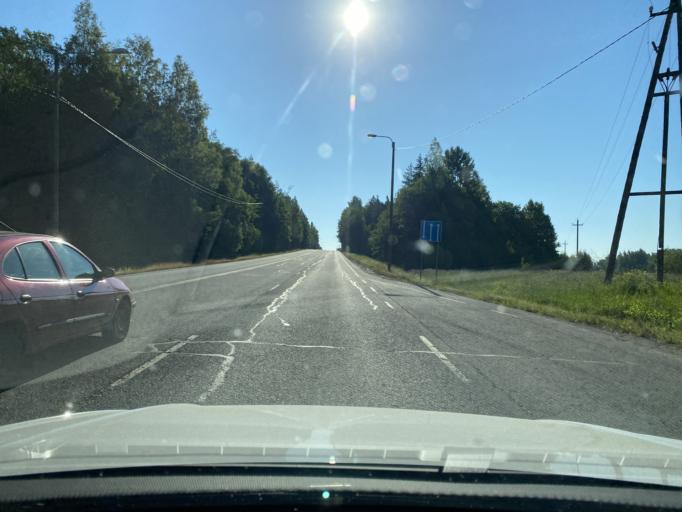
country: FI
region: Haeme
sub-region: Forssa
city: Forssa
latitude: 60.8281
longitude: 23.6399
